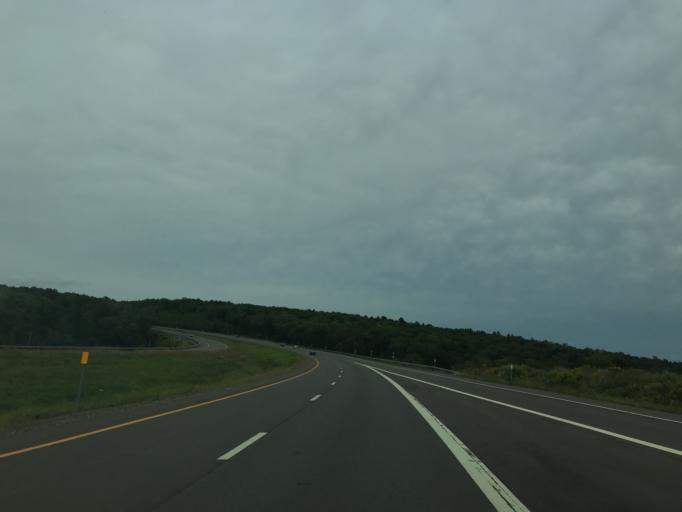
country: US
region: New York
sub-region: Chenango County
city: Greene
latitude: 42.1855
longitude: -75.6976
